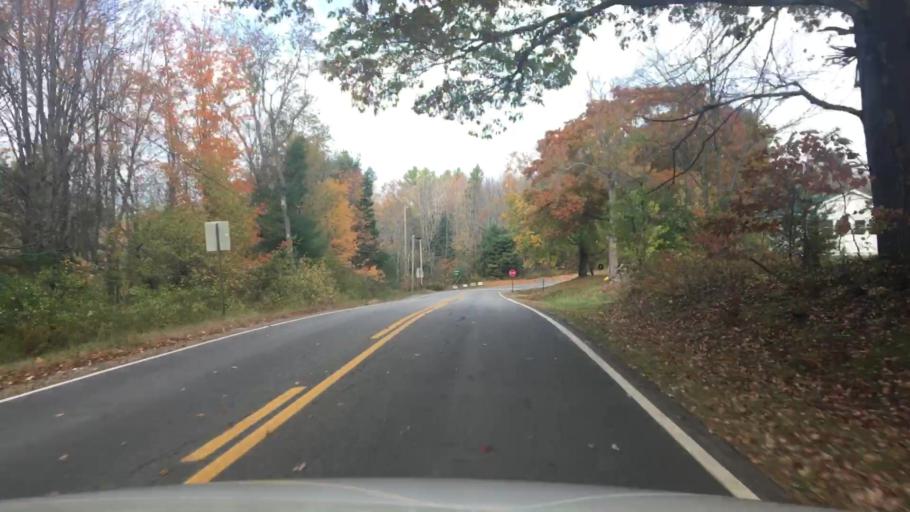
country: US
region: Maine
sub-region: Waldo County
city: Searsmont
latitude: 44.3619
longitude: -69.1479
